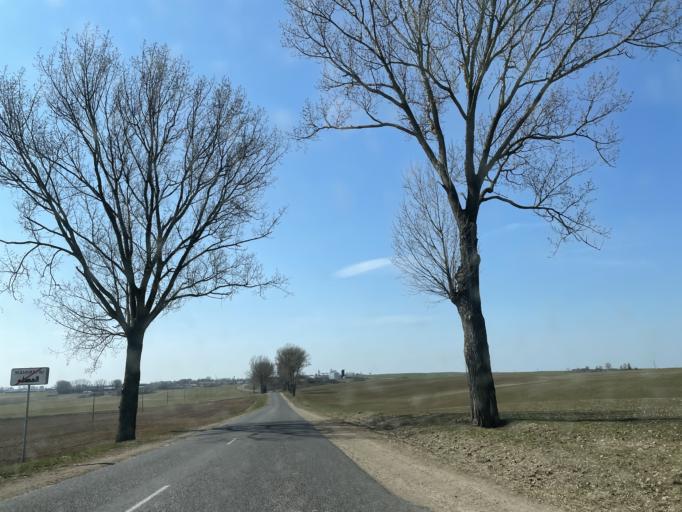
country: BY
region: Minsk
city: Snow
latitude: 53.1979
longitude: 26.4969
